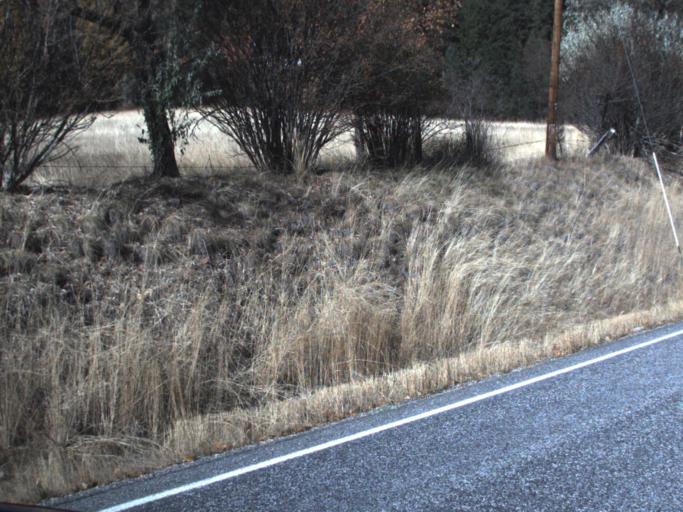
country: CA
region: British Columbia
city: Grand Forks
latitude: 48.9247
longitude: -118.5666
